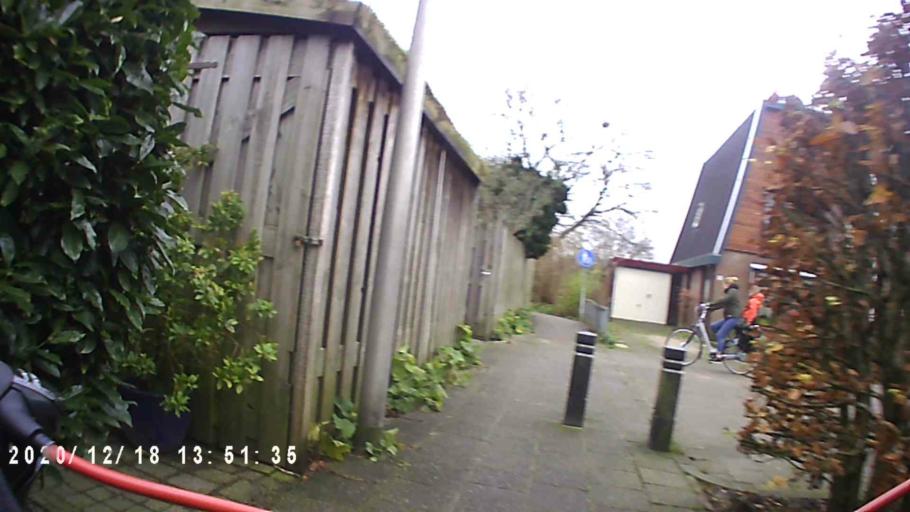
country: NL
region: Groningen
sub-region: Gemeente Bedum
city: Bedum
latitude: 53.2984
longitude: 6.6085
